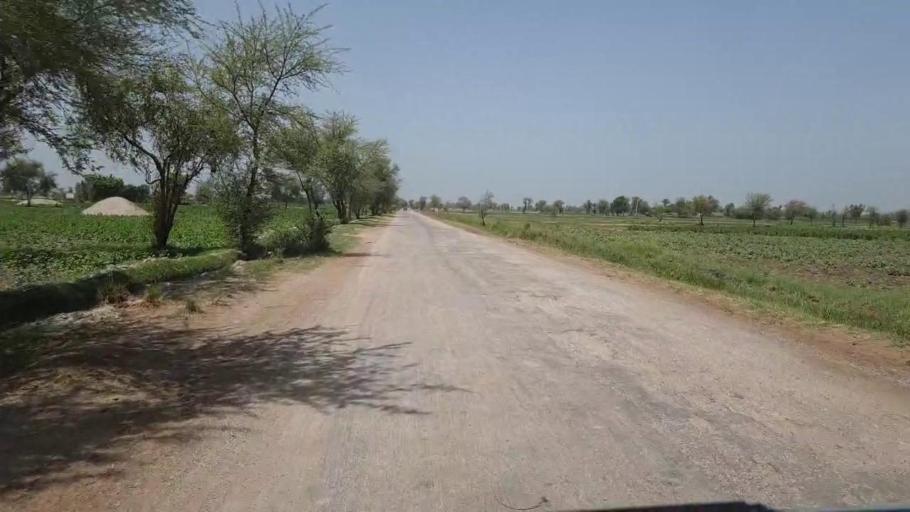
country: PK
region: Sindh
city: Nawabshah
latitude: 26.3511
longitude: 68.3940
